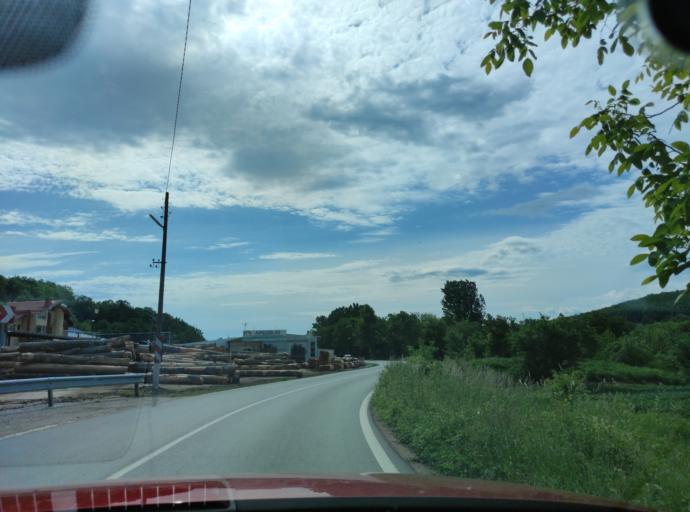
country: BG
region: Montana
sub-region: Obshtina Chiprovtsi
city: Chiprovtsi
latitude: 43.4398
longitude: 22.9372
